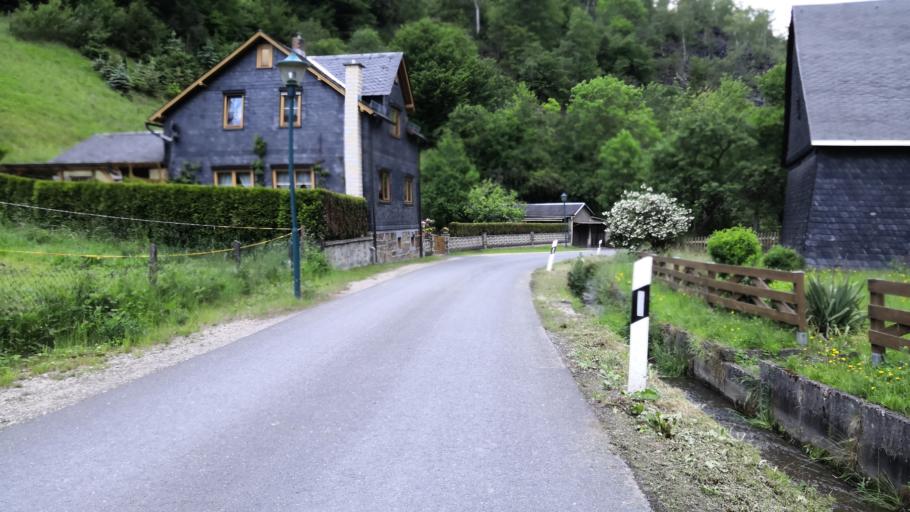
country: DE
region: Thuringia
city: Probstzella
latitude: 50.5664
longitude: 11.3763
